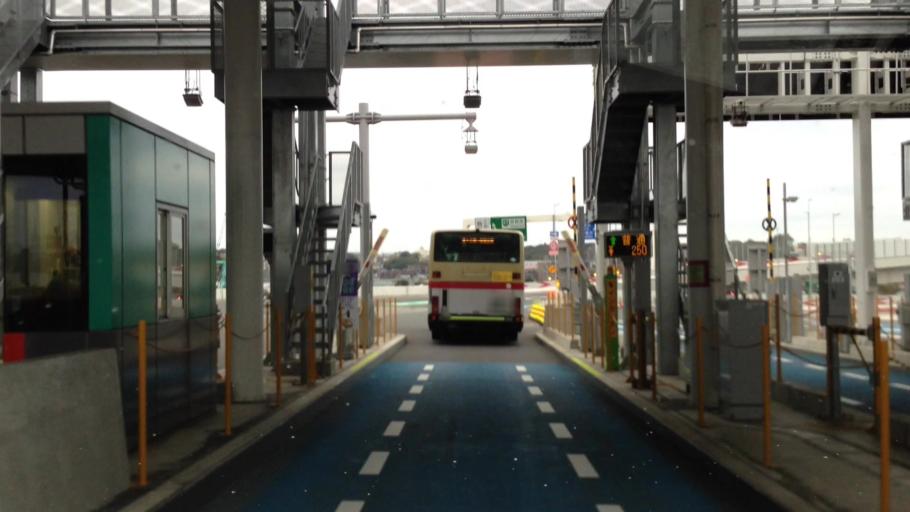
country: JP
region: Kanagawa
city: Yokohama
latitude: 35.5170
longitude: 139.5922
